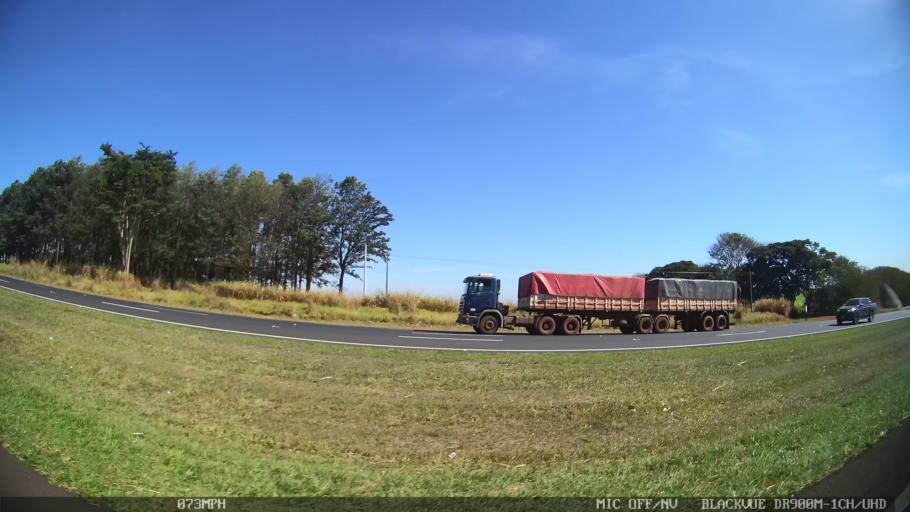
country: BR
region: Sao Paulo
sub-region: Cravinhos
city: Cravinhos
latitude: -21.2968
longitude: -47.7440
